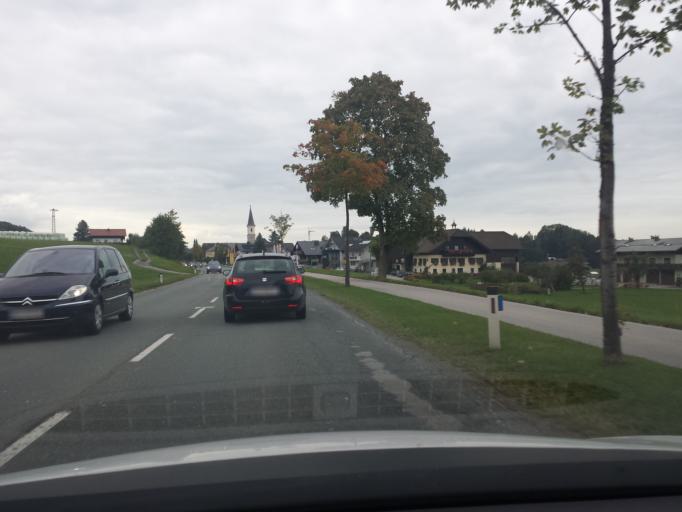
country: AT
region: Salzburg
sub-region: Politischer Bezirk Salzburg-Umgebung
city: Hof bei Salzburg
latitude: 47.8188
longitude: 13.2215
